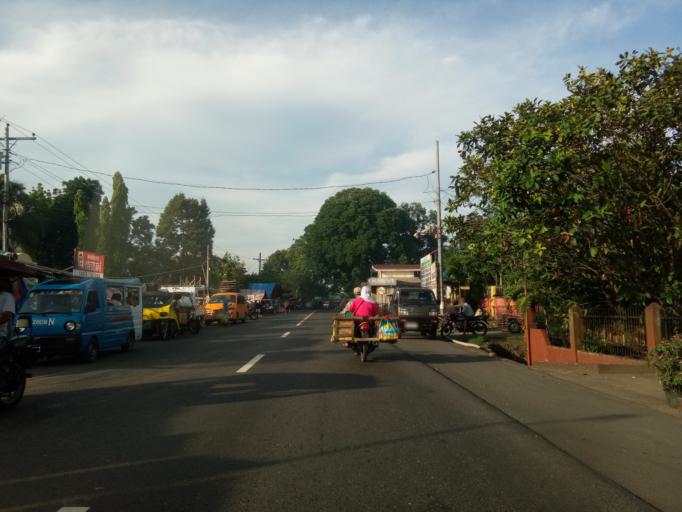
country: PH
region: Caraga
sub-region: Province of Surigao del Norte
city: Tubod
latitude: 9.5569
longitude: 125.5693
